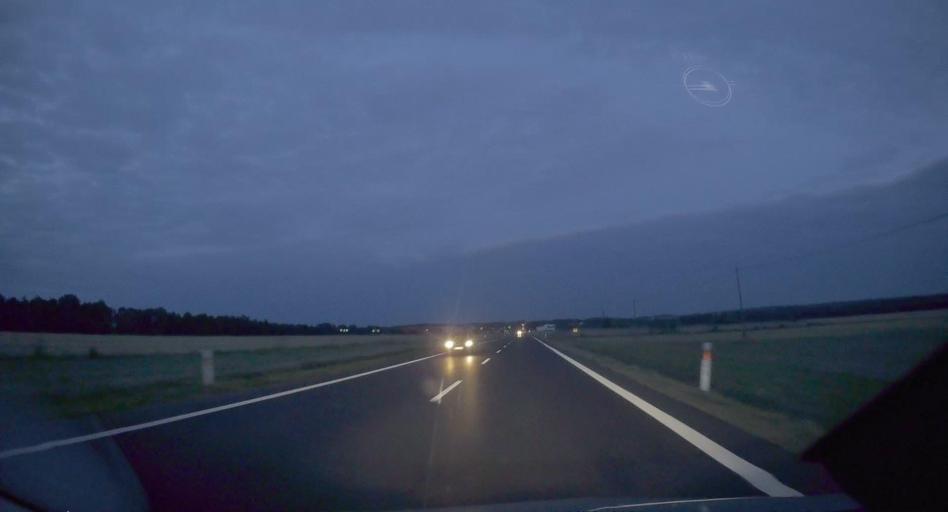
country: PL
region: Silesian Voivodeship
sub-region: Powiat klobucki
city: Klobuck
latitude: 50.8905
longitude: 18.9665
